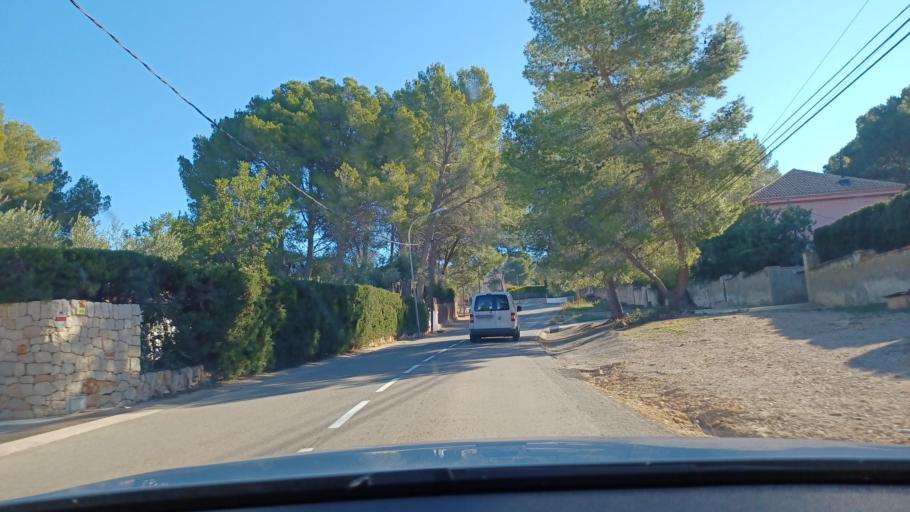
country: ES
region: Catalonia
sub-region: Provincia de Tarragona
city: Tortosa
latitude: 40.8134
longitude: 0.5410
